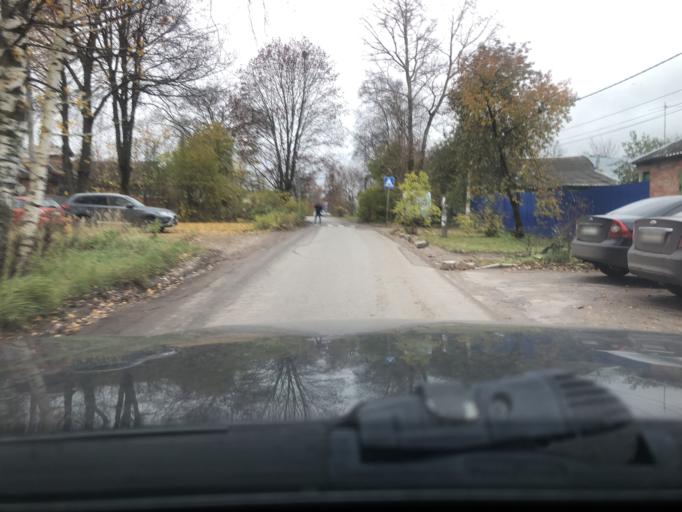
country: RU
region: Moskovskaya
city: Sergiyev Posad
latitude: 56.2943
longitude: 38.1124
